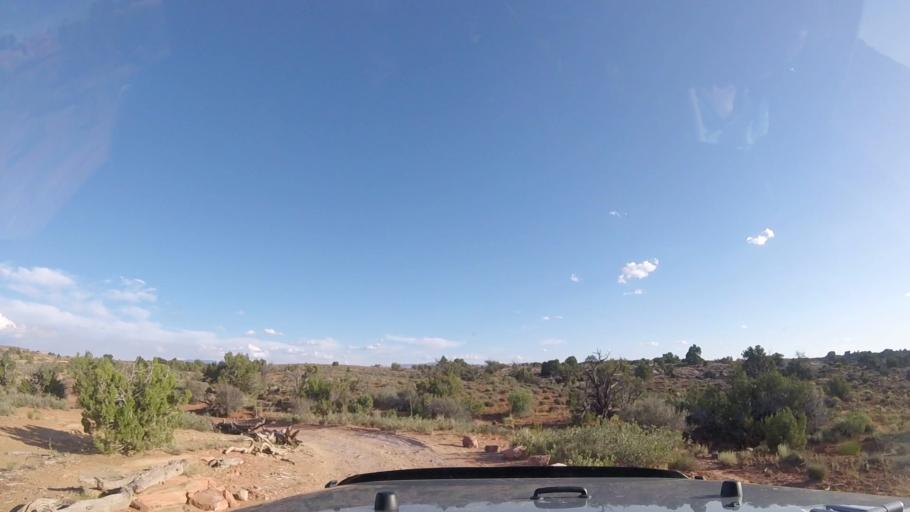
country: US
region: Utah
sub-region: Grand County
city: Moab
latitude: 38.2085
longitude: -109.7873
